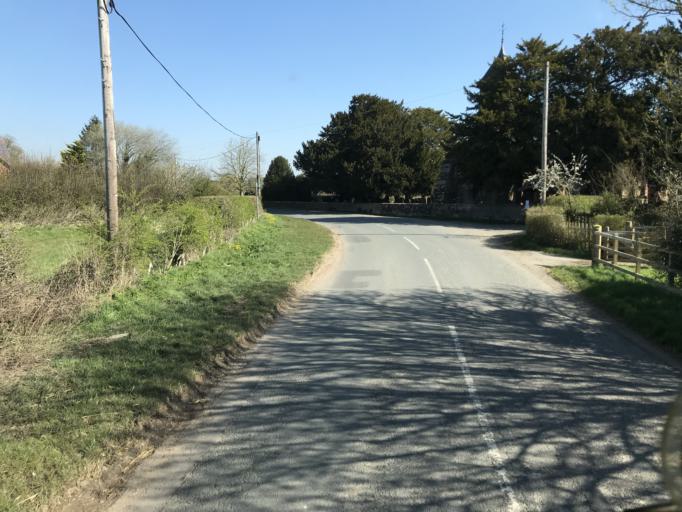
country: GB
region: England
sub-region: Cheshire West and Chester
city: Aldford
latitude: 53.1388
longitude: -2.8428
